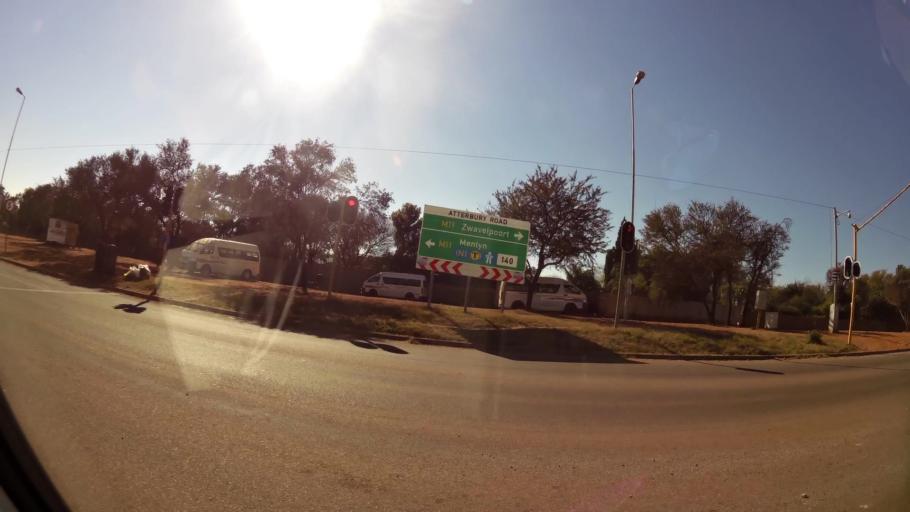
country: ZA
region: Gauteng
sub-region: City of Tshwane Metropolitan Municipality
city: Pretoria
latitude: -25.7891
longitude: 28.3093
